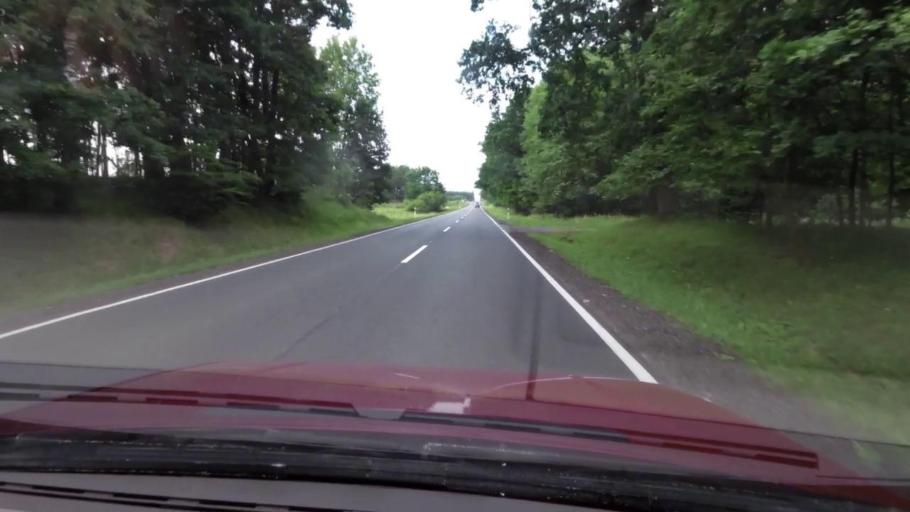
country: PL
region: Pomeranian Voivodeship
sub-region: Powiat bytowski
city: Trzebielino
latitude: 54.2351
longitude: 17.0902
